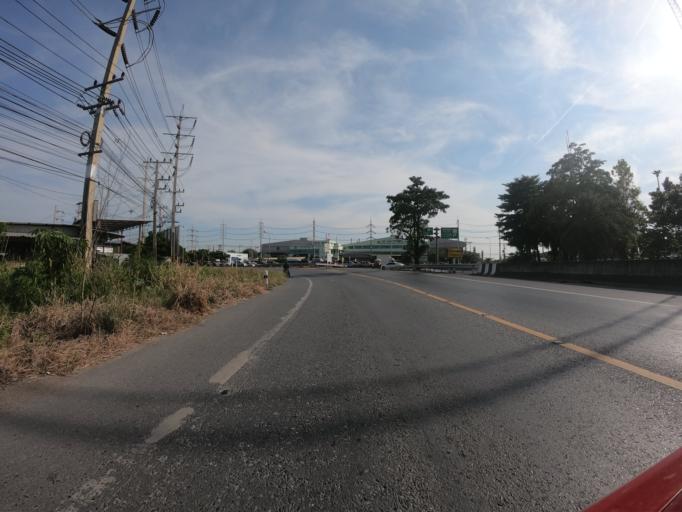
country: TH
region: Pathum Thani
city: Lam Luk Ka
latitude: 13.9344
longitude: 100.7105
